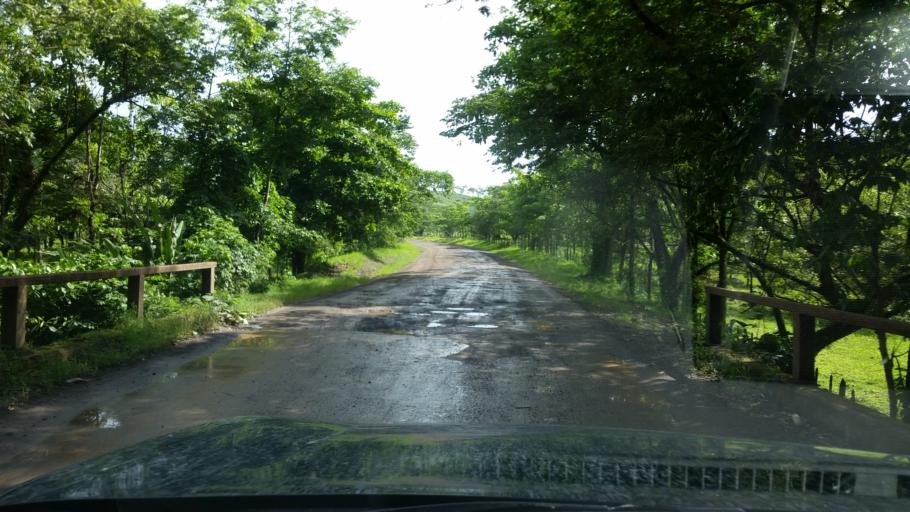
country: NI
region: Atlantico Norte (RAAN)
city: Siuna
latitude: 13.6902
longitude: -84.7883
